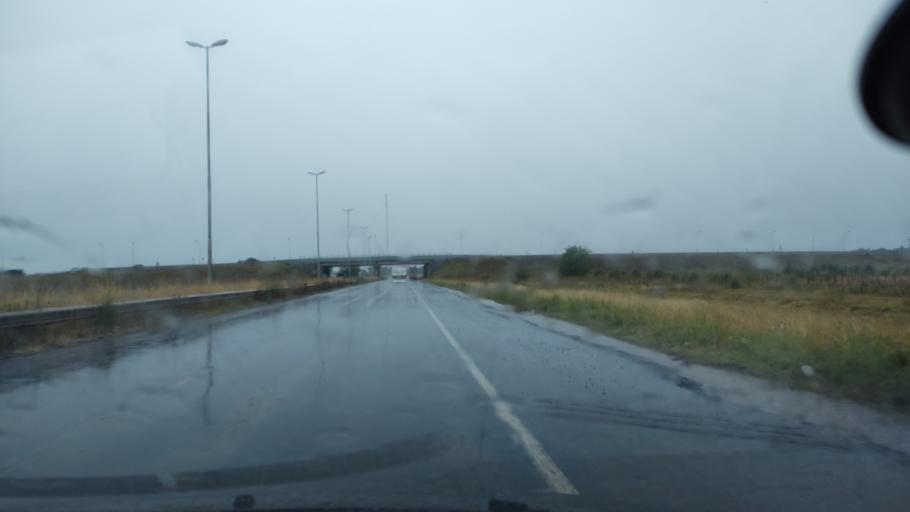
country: AR
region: Buenos Aires
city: Canuelas
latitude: -35.0208
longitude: -58.7447
